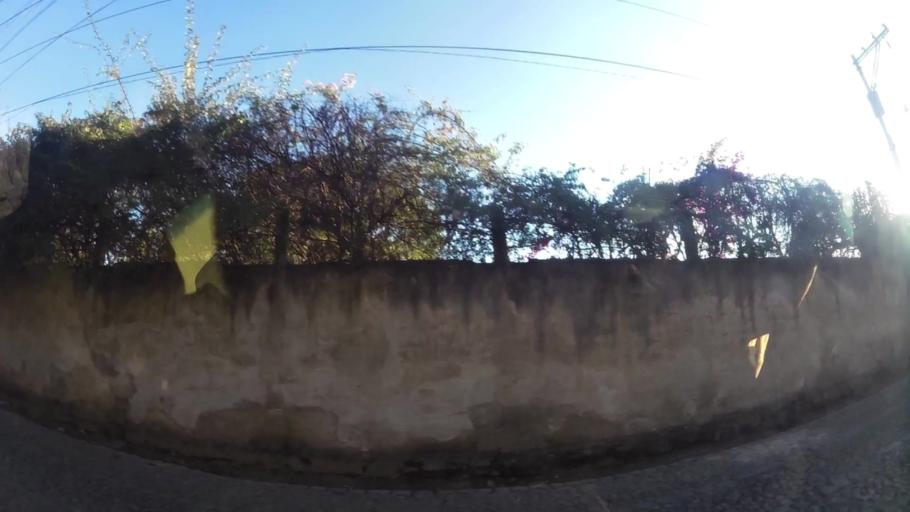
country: GT
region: Sacatepequez
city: Antigua Guatemala
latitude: 14.5629
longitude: -90.7320
